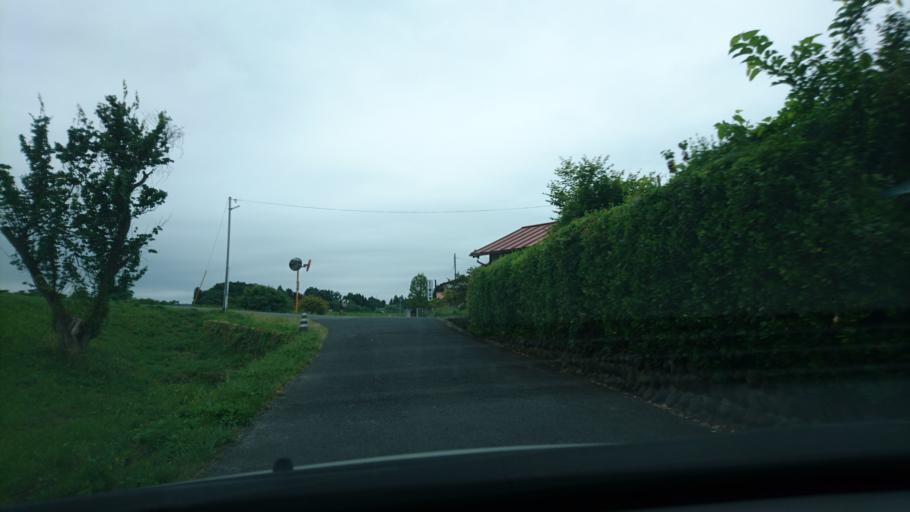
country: JP
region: Iwate
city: Ichinoseki
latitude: 38.9260
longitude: 141.1215
